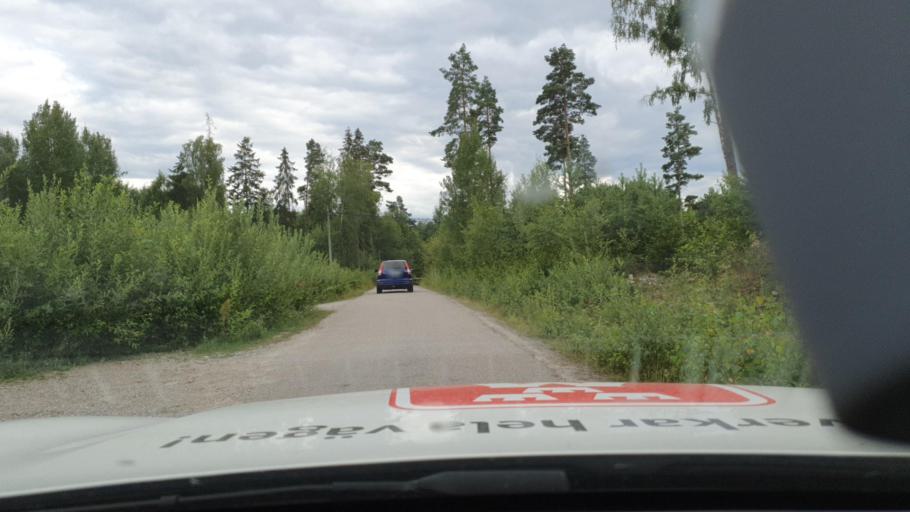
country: SE
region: Soedermanland
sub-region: Strangnas Kommun
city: Stallarholmen
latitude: 59.4082
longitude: 17.3067
